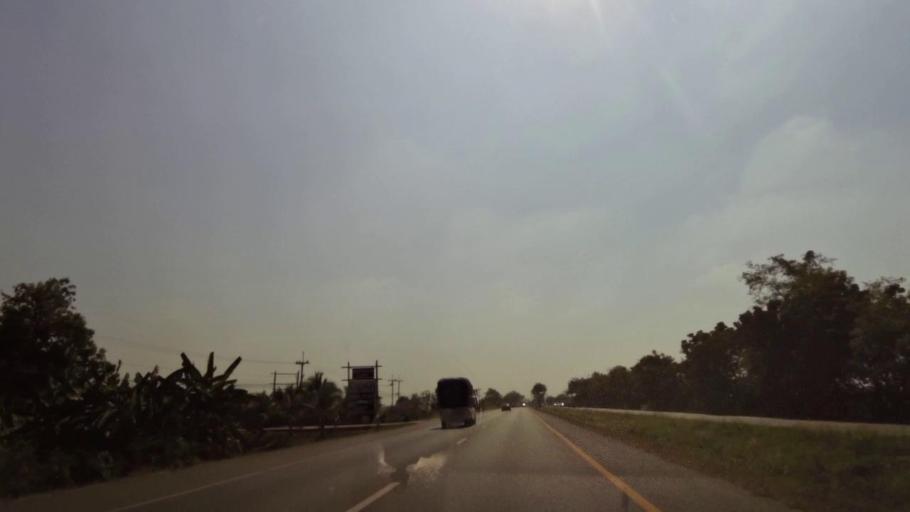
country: TH
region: Phichit
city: Wachira Barami
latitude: 16.4755
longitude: 100.1472
